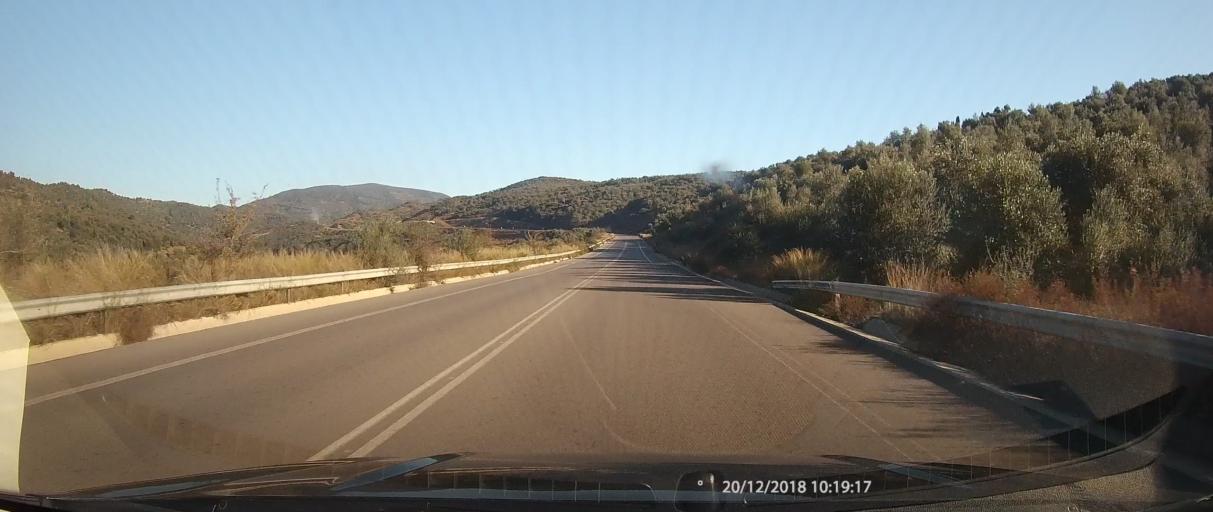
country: GR
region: Peloponnese
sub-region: Nomos Lakonias
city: Magoula
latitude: 37.1319
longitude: 22.4207
